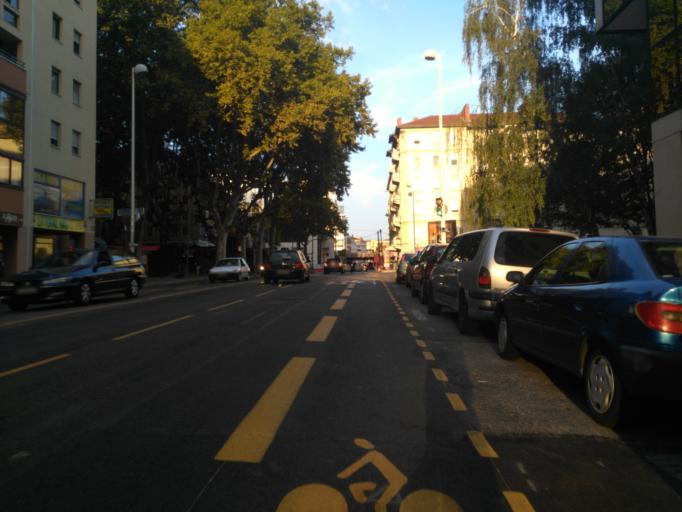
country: FR
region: Rhone-Alpes
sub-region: Departement du Rhone
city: Lyon
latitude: 45.7567
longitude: 4.8573
